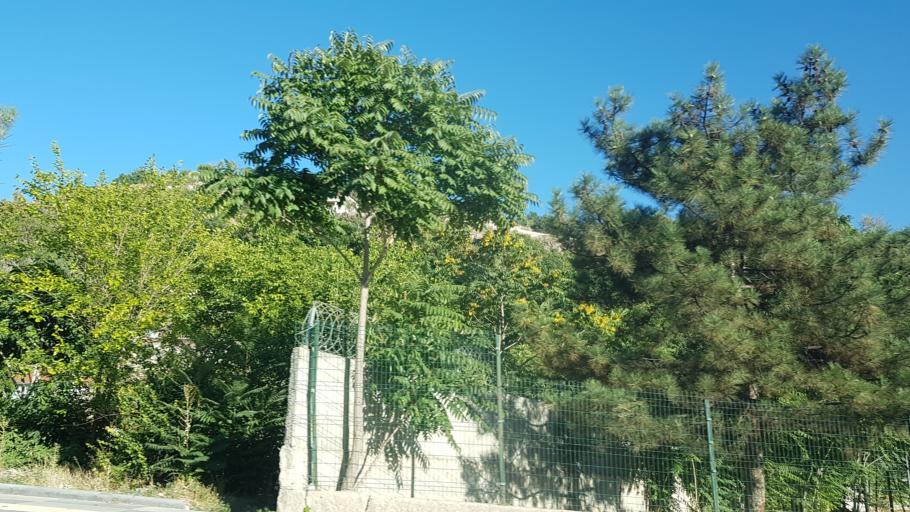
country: TR
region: Ankara
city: Ankara
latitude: 39.9471
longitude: 32.8614
